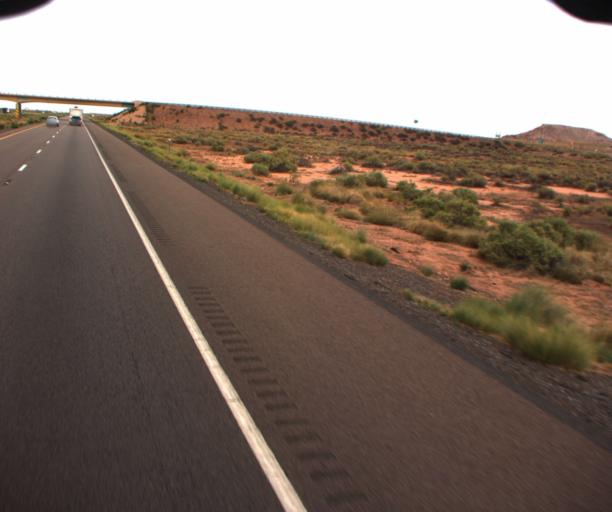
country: US
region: Arizona
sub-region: Coconino County
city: LeChee
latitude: 35.0669
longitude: -110.8331
